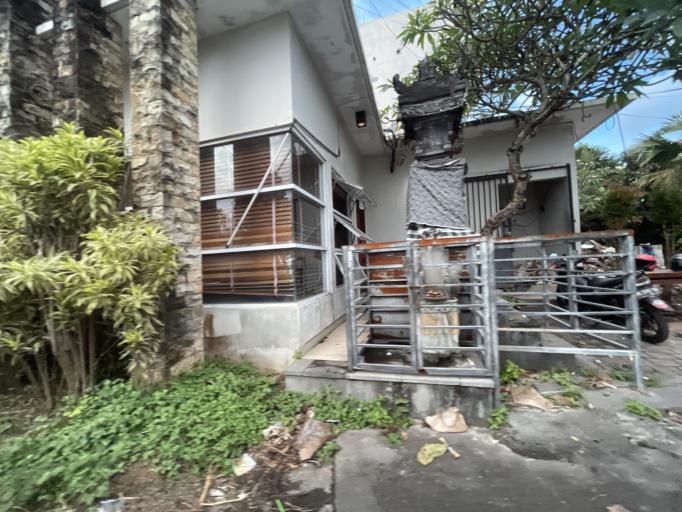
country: ID
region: Bali
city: Kuta
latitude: -8.6753
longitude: 115.1694
